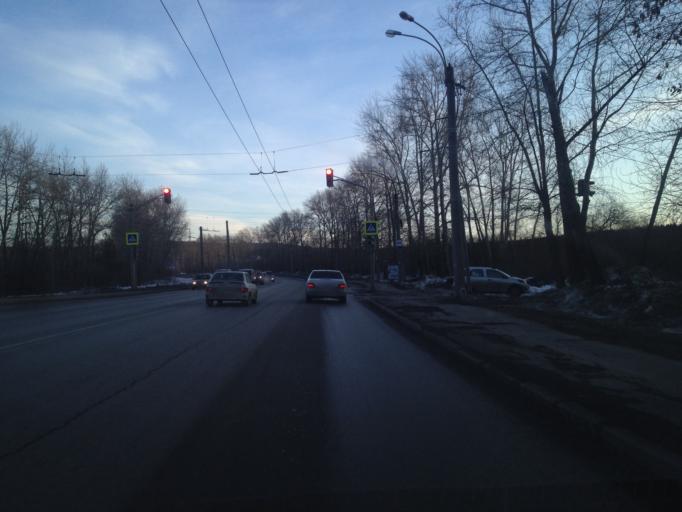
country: RU
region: Sverdlovsk
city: Yekaterinburg
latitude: 56.7622
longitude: 60.6719
